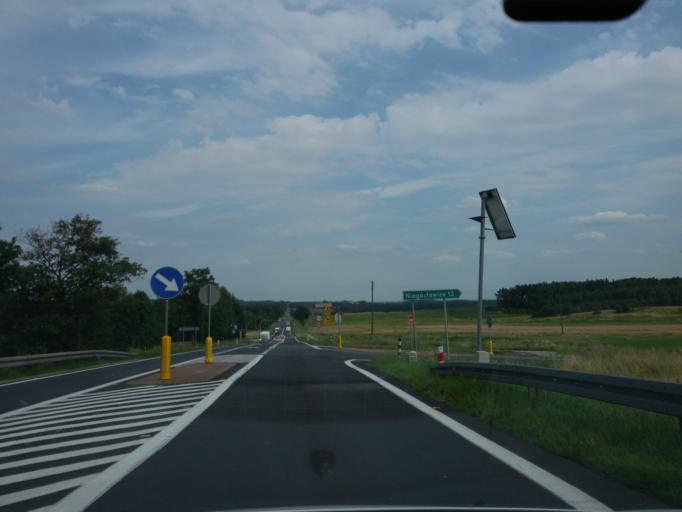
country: PL
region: Lower Silesian Voivodeship
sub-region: Powiat polkowicki
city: Gaworzyce
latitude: 51.6611
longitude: 15.8231
